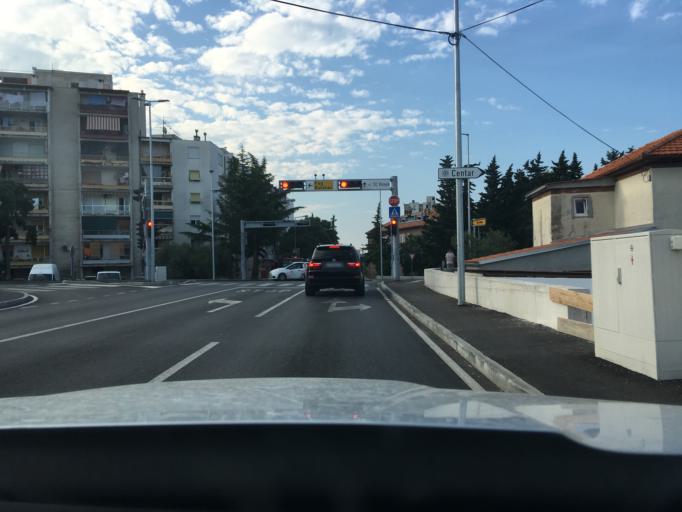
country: HR
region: Zadarska
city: Zadar
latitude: 44.1266
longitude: 15.2341
